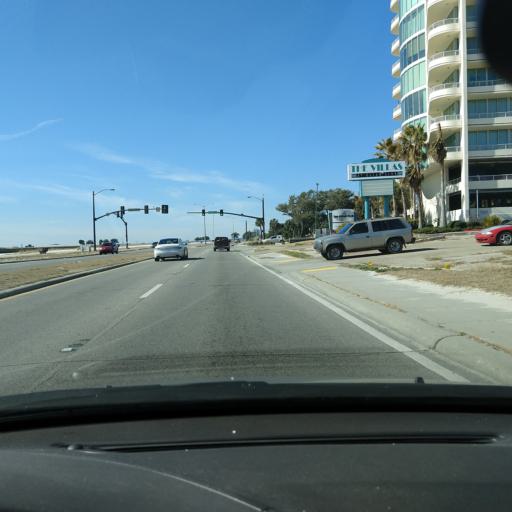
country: US
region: Mississippi
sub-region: Harrison County
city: Biloxi
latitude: 30.3923
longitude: -88.9583
